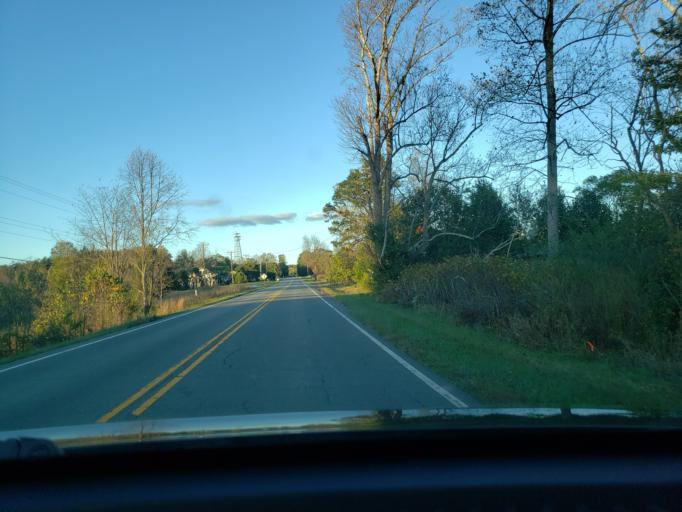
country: US
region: North Carolina
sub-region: Stokes County
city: Danbury
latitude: 36.3323
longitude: -80.2245
